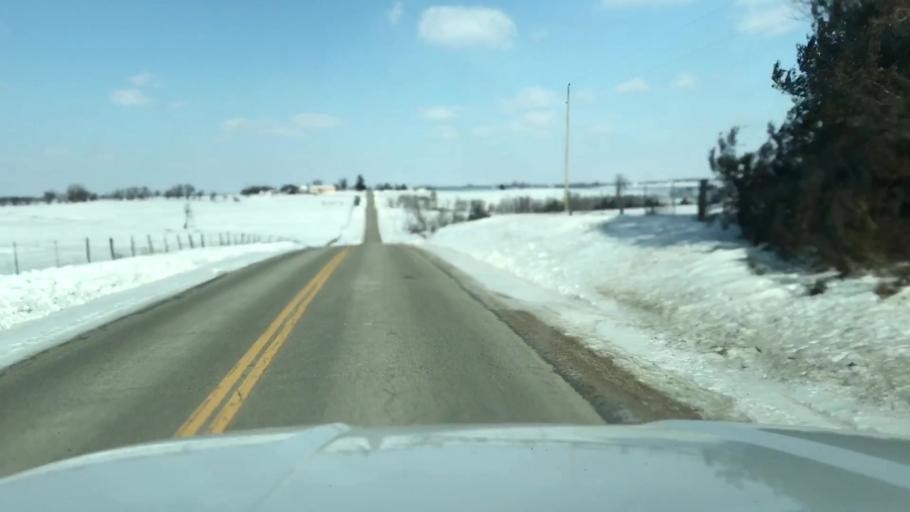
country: US
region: Missouri
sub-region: Nodaway County
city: Maryville
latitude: 40.3737
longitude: -94.7215
